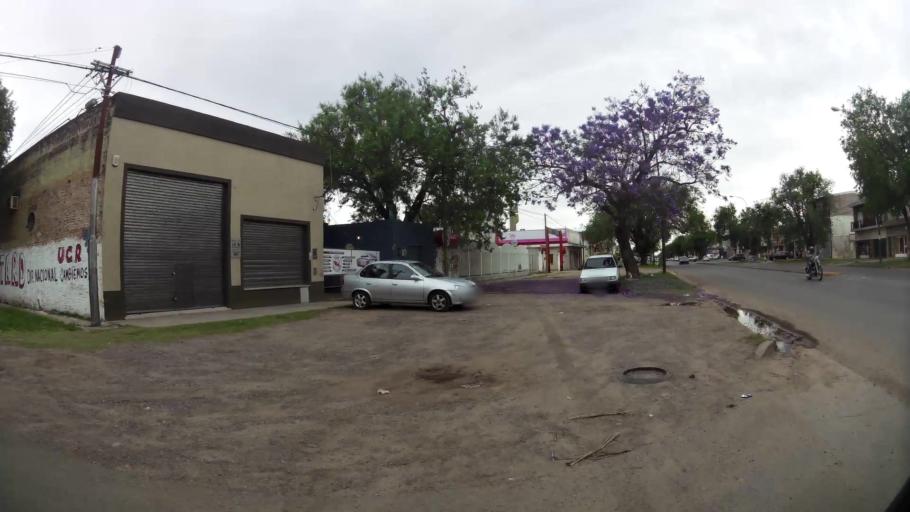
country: AR
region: Santa Fe
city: Gobernador Galvez
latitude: -32.9987
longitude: -60.6750
